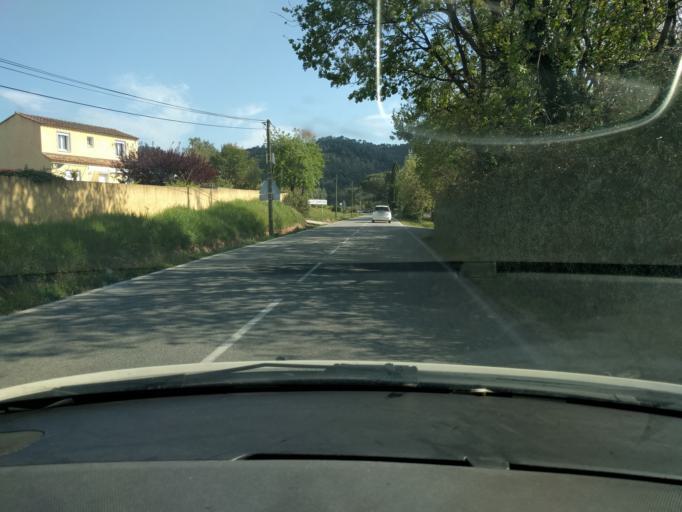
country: FR
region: Provence-Alpes-Cote d'Azur
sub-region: Departement du Var
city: Pierrefeu-du-Var
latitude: 43.2208
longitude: 6.1429
